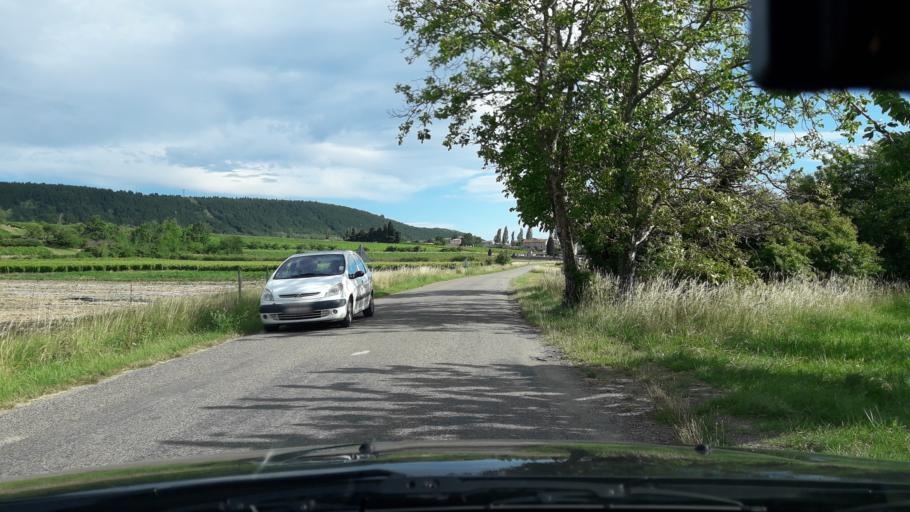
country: FR
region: Rhone-Alpes
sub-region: Departement de l'Ardeche
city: Lavilledieu
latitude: 44.6170
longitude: 4.4745
